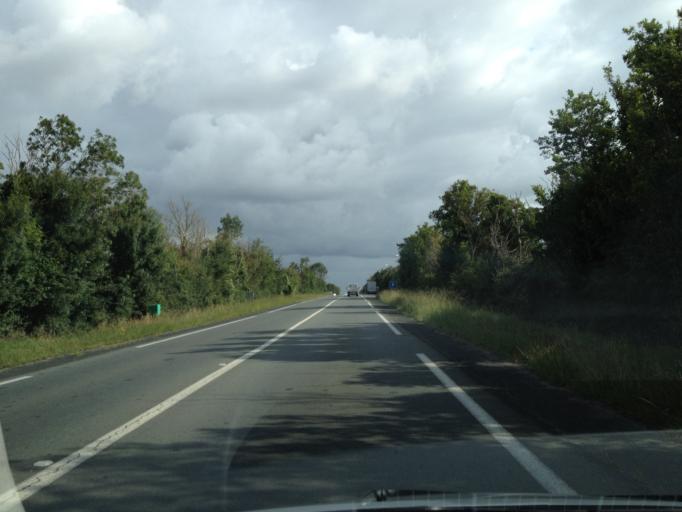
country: FR
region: Poitou-Charentes
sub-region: Departement de la Charente-Maritime
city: Sainte-Soulle
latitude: 46.2209
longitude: -1.0226
